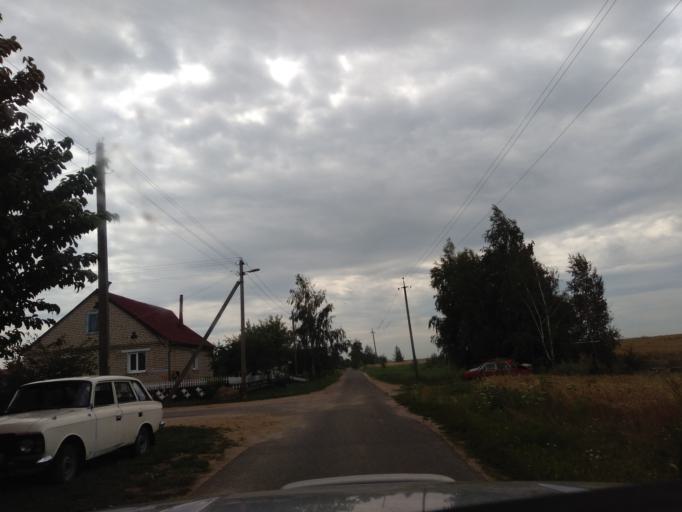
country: BY
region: Minsk
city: Kapyl'
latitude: 53.1562
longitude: 27.0665
